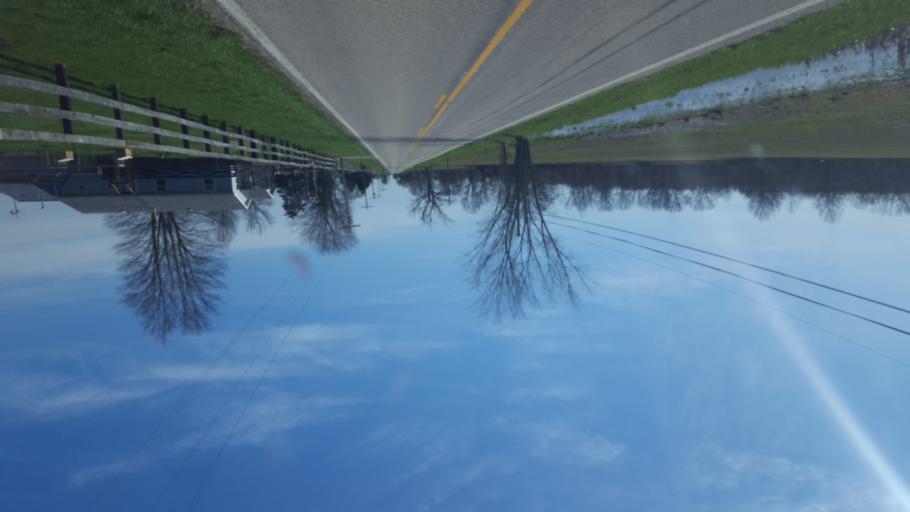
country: US
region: Ohio
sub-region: Morrow County
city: Cardington
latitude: 40.5359
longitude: -82.9626
